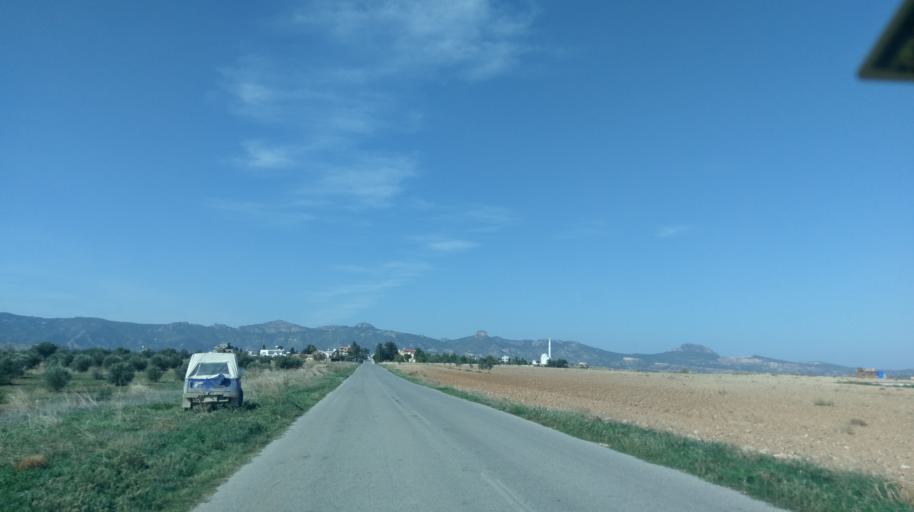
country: CY
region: Ammochostos
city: Trikomo
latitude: 35.3485
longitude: 33.9668
